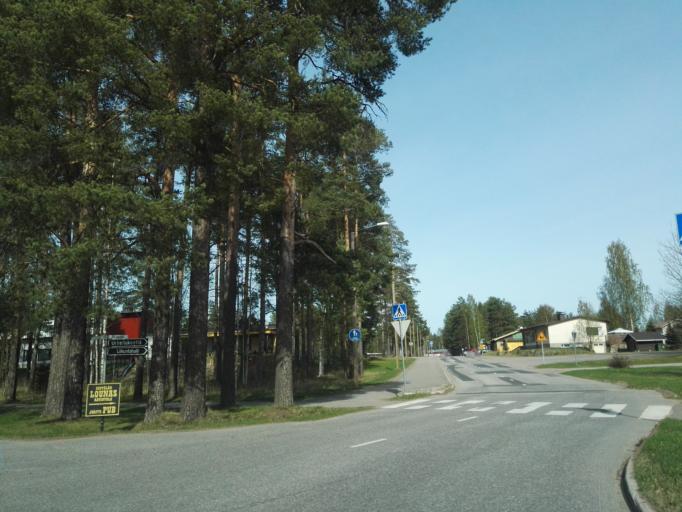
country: FI
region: Central Finland
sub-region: Joutsa
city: Joutsa
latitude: 61.7451
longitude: 26.1203
